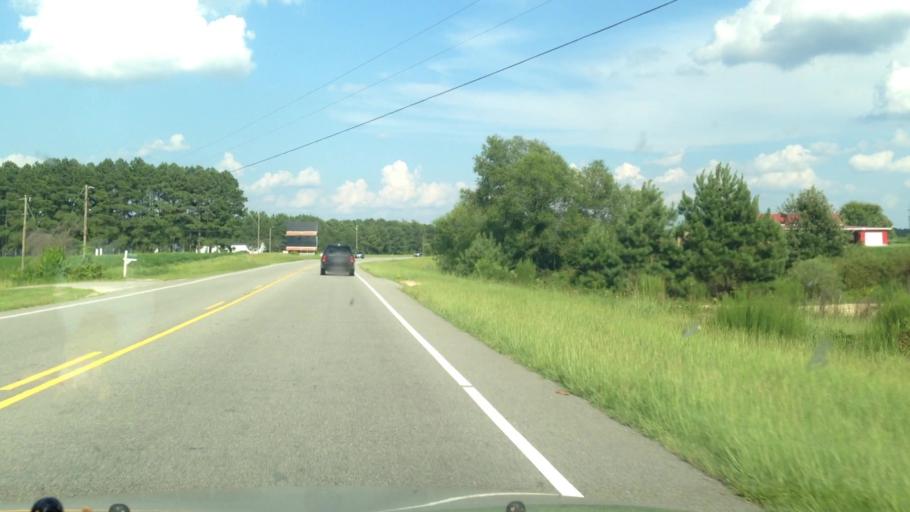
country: US
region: North Carolina
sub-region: Harnett County
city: Lillington
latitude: 35.4184
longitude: -78.8827
